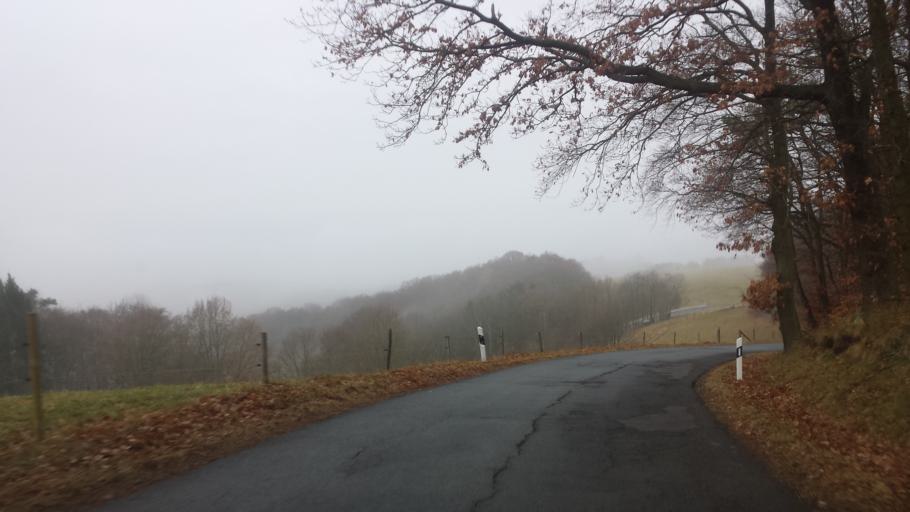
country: DE
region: Hesse
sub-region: Regierungsbezirk Darmstadt
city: Seeheim-Jugenheim
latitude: 49.7561
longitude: 8.6870
